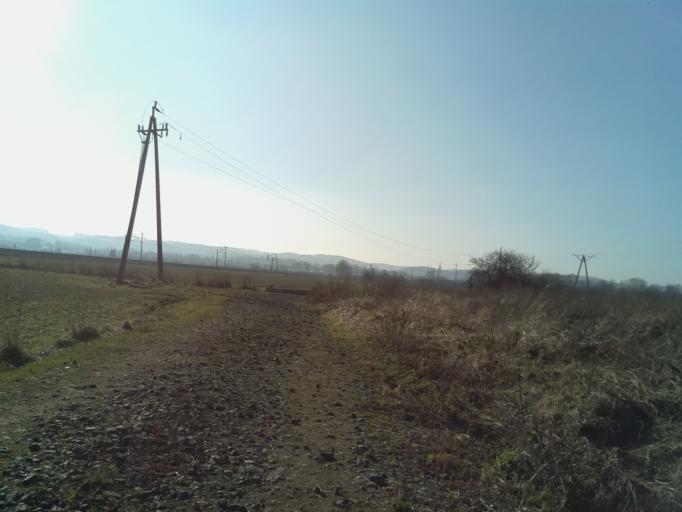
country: PL
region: Lower Silesian Voivodeship
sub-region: Powiat swidnicki
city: Swiebodzice
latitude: 50.8689
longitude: 16.3431
